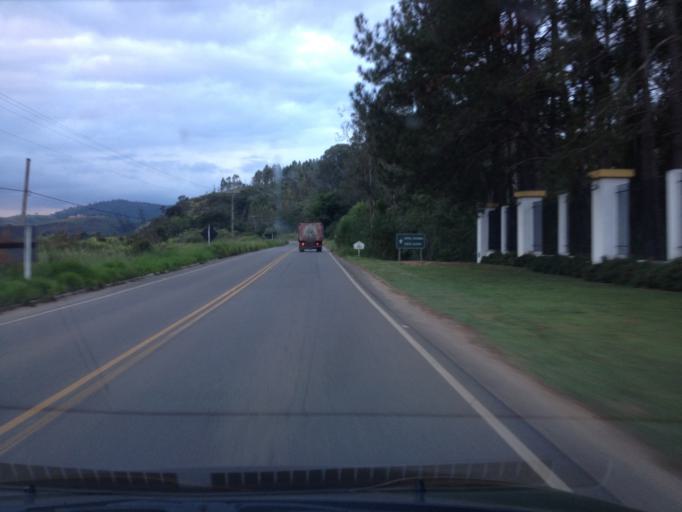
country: BR
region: Minas Gerais
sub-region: Sao Lourenco
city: Sao Lourenco
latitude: -22.0914
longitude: -45.0423
